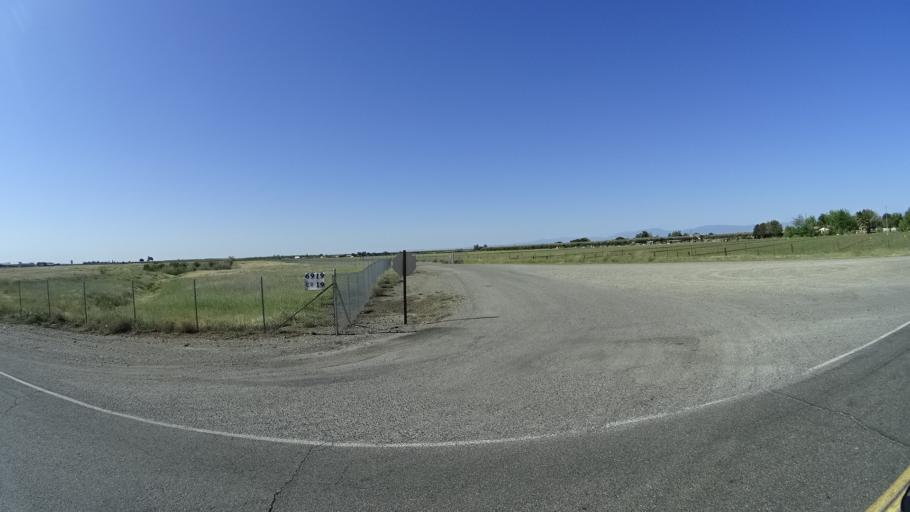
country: US
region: California
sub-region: Glenn County
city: Orland
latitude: 39.7287
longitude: -122.1496
